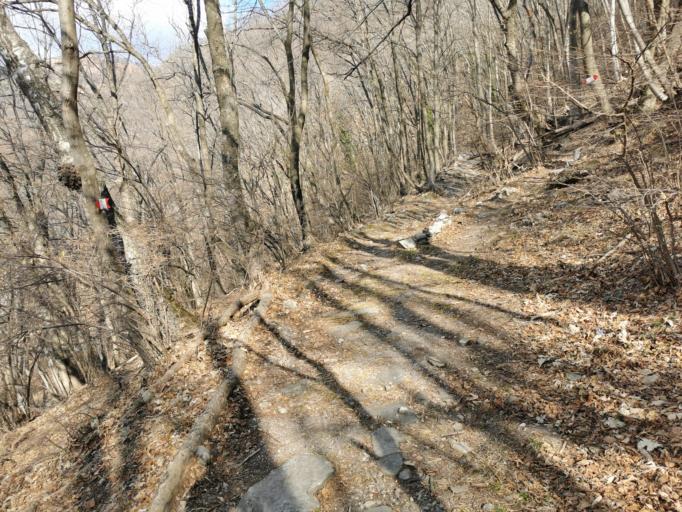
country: IT
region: Lombardy
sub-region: Provincia di Como
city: Carate Urio
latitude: 45.8844
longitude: 9.1174
